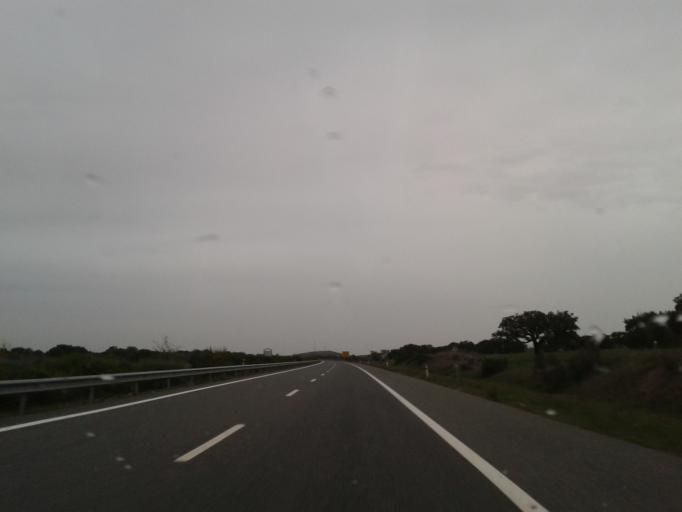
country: PT
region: Beja
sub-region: Ourique
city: Ourique
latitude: 37.6859
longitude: -8.1652
